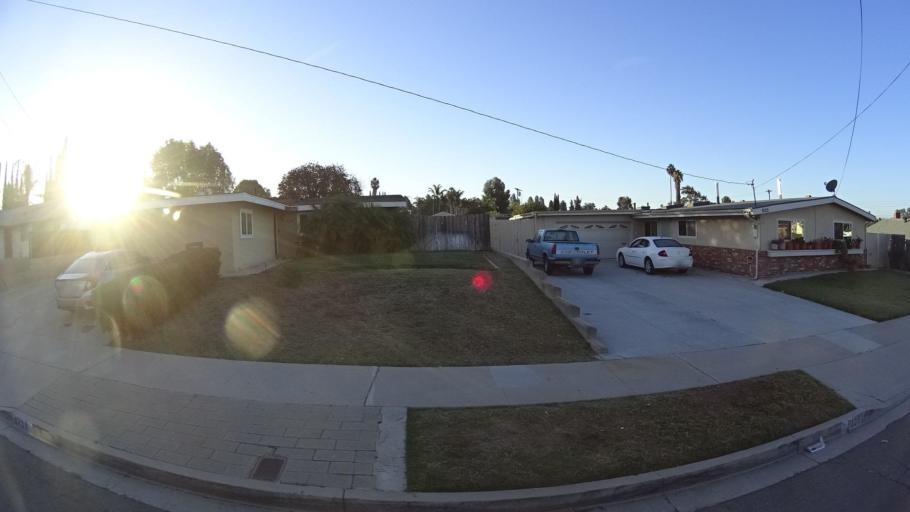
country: US
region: California
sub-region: San Diego County
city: La Presa
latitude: 32.7093
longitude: -117.0031
